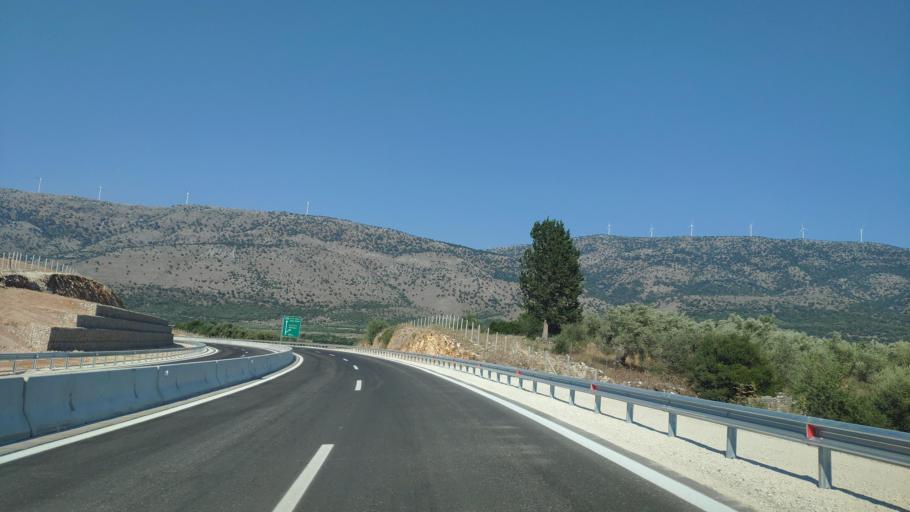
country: GR
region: West Greece
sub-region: Nomos Aitolias kai Akarnanias
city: Stanos
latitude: 38.7720
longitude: 21.1777
